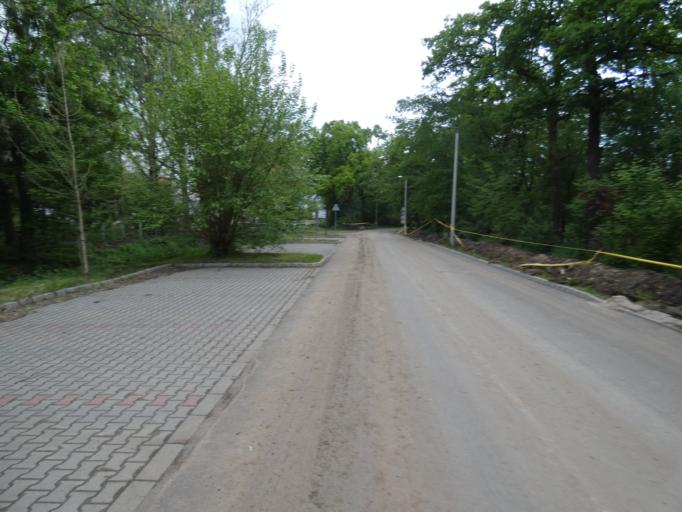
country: HU
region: Szabolcs-Szatmar-Bereg
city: Kotaj
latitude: 48.0078
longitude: 21.7212
